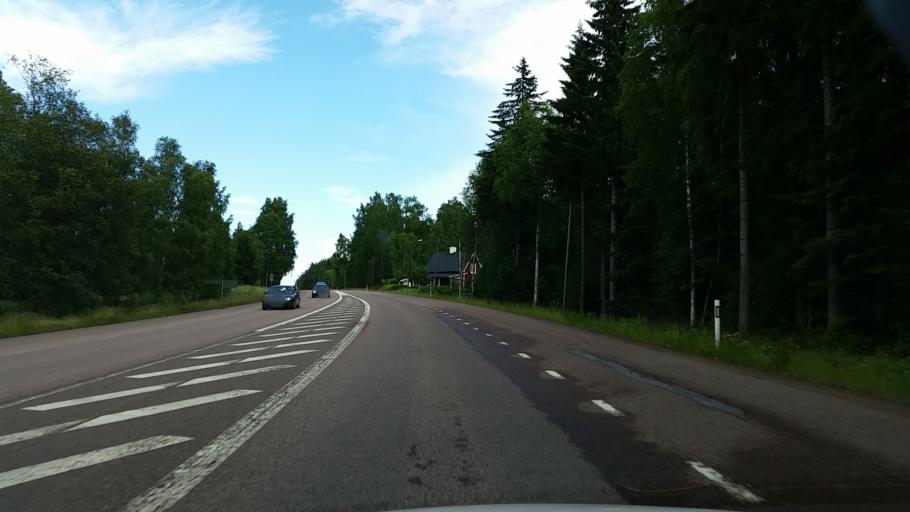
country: SE
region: Dalarna
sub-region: Smedjebackens Kommun
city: Smedjebacken
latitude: 60.1405
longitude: 15.3437
